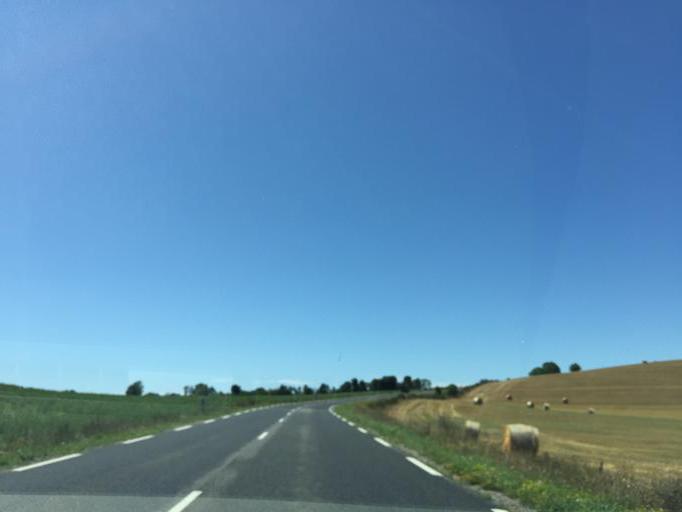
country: FR
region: Midi-Pyrenees
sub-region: Departement de l'Aveyron
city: Salles-Curan
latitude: 44.2419
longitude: 2.8636
